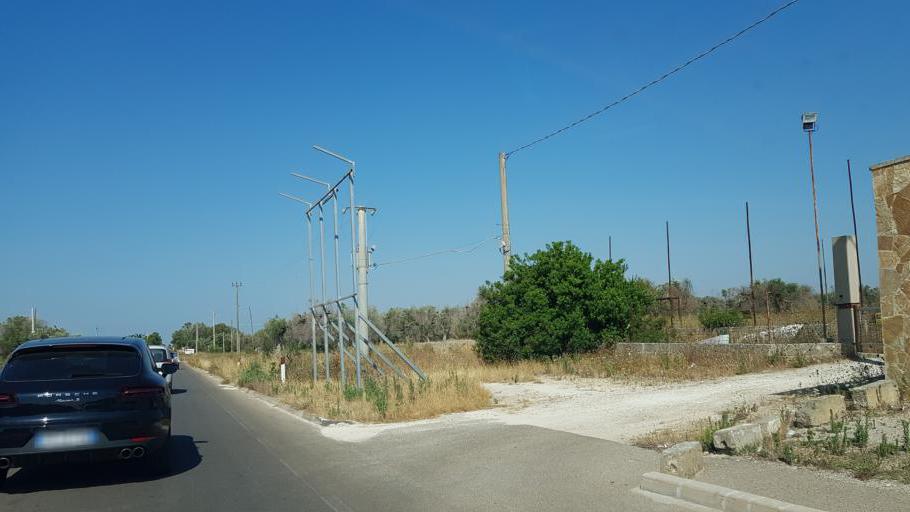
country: IT
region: Apulia
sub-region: Provincia di Lecce
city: Veglie
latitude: 40.3283
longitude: 17.9338
